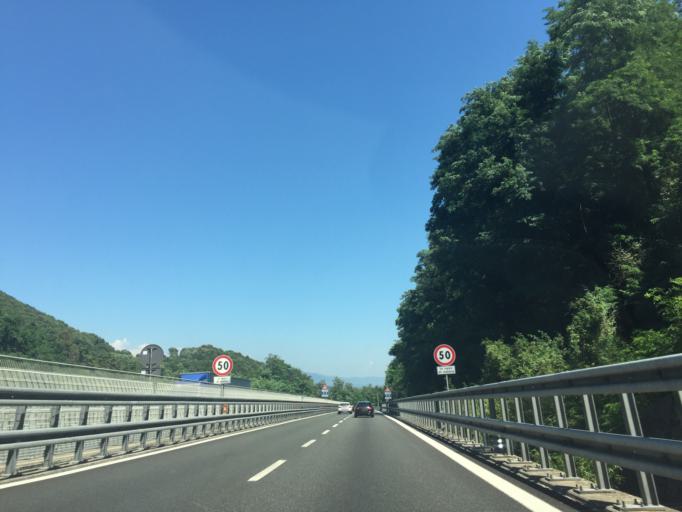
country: IT
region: Tuscany
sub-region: Province of Pisa
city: Filettole
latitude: 43.8531
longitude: 10.3906
